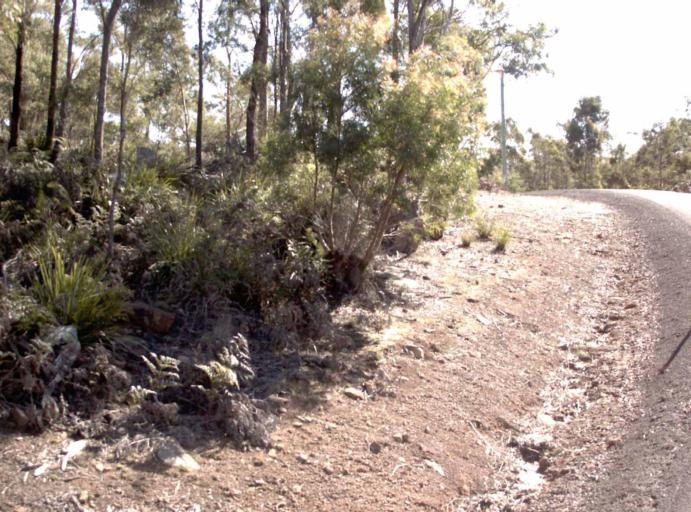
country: AU
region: Tasmania
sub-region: Launceston
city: Mayfield
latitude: -41.3183
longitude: 147.1192
